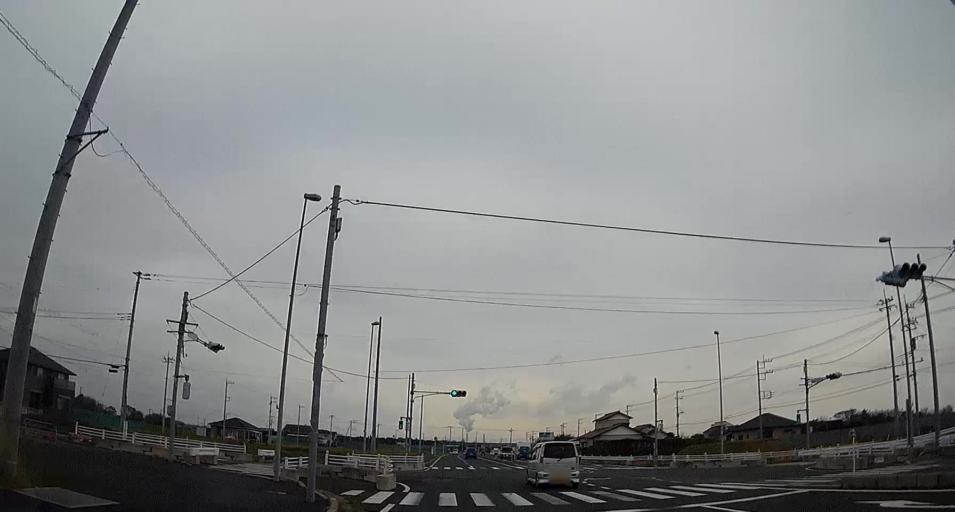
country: JP
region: Chiba
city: Kisarazu
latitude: 35.4258
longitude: 139.9221
